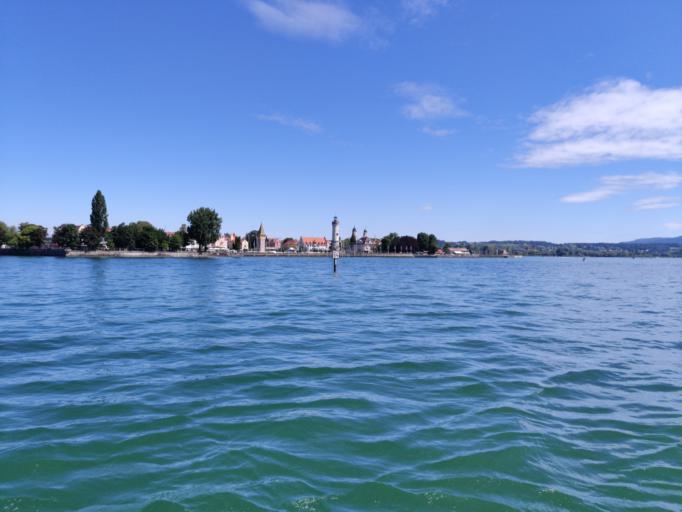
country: DE
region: Bavaria
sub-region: Swabia
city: Lindau
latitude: 47.5394
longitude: 9.6808
